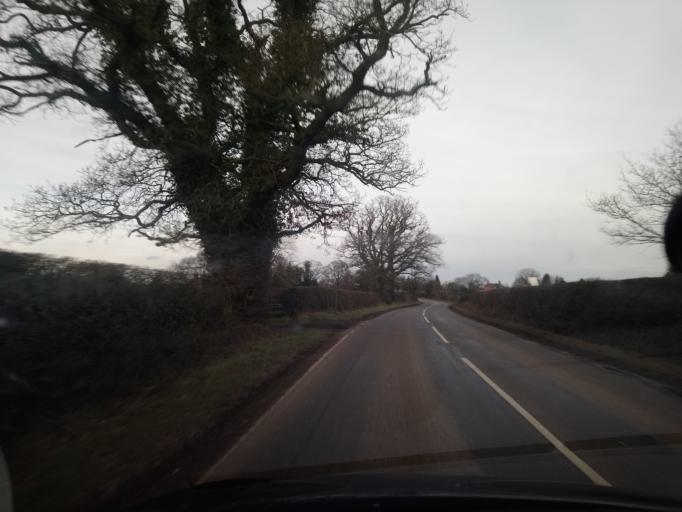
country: GB
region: England
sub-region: Shropshire
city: Prees
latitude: 52.9101
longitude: -2.6874
